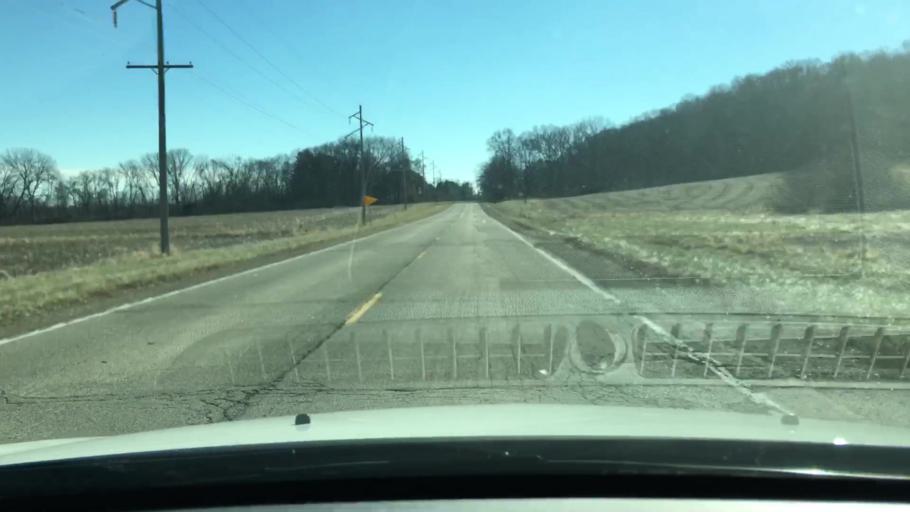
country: US
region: Illinois
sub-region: Fulton County
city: Astoria
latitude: 40.2086
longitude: -90.2052
